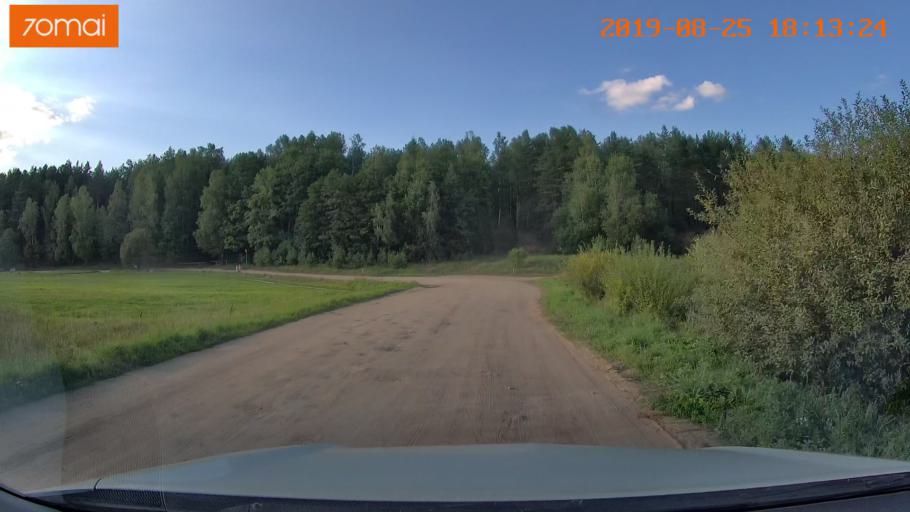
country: BY
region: Minsk
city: Khatsyezhyna
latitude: 53.9438
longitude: 27.3068
